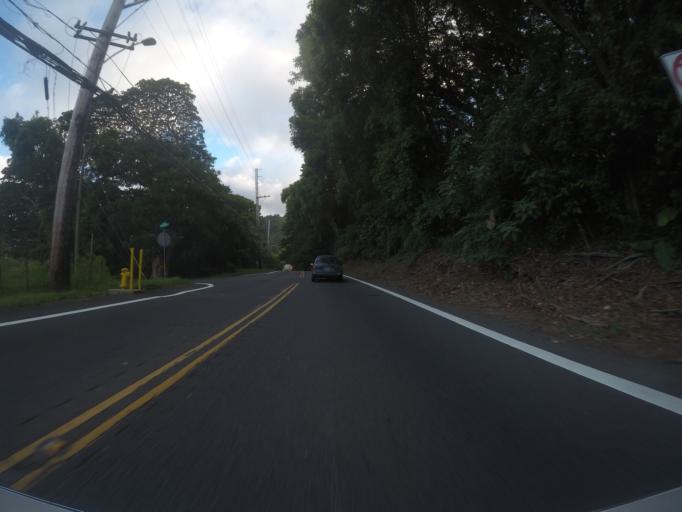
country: US
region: Hawaii
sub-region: Honolulu County
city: Ka'a'awa
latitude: 21.5097
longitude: -157.8540
